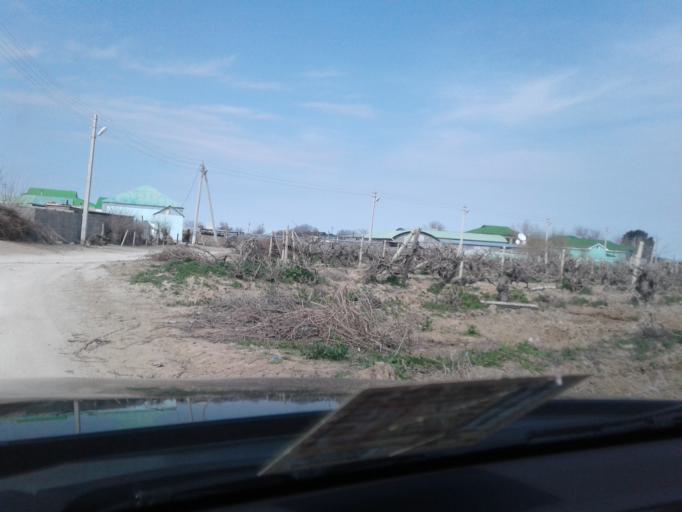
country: TM
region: Ahal
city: Abadan
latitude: 38.1164
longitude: 58.3524
